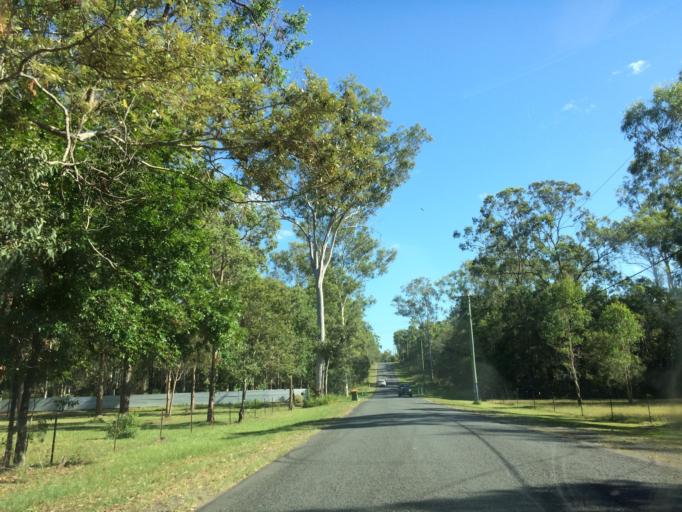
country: AU
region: Queensland
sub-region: Ipswich
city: Springfield Lakes
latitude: -27.7091
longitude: 152.9568
